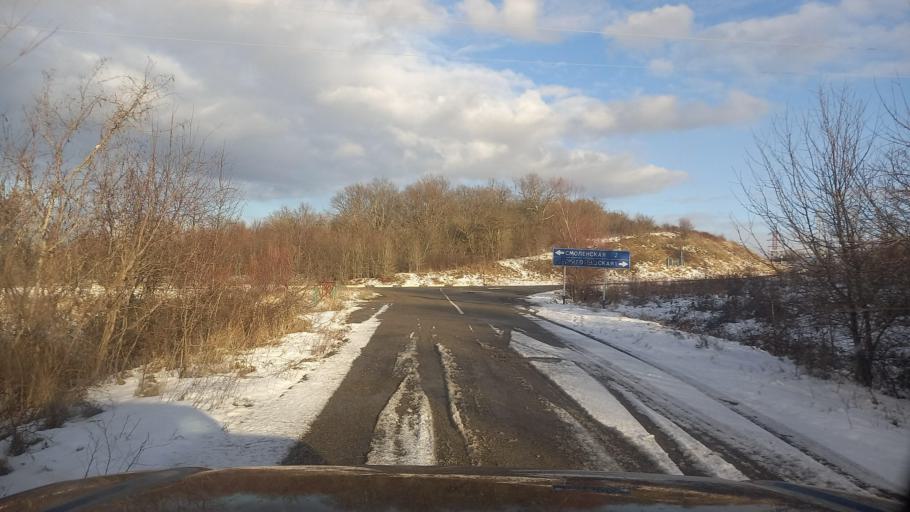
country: RU
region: Krasnodarskiy
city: Smolenskaya
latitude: 44.7719
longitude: 38.8172
